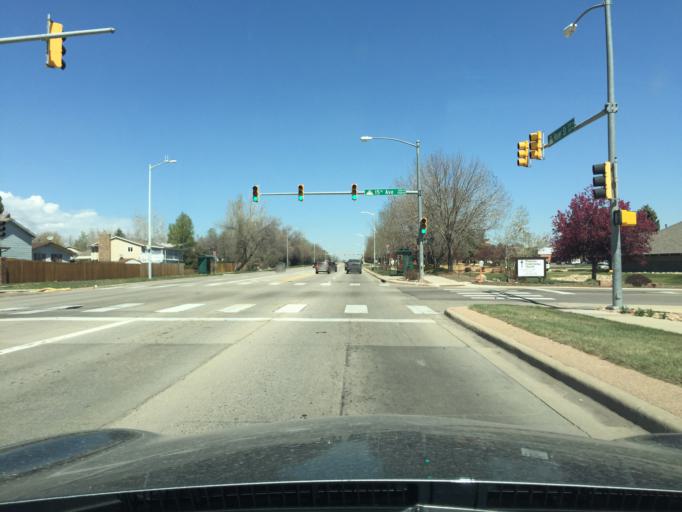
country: US
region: Colorado
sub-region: Boulder County
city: Longmont
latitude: 40.1847
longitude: -105.1308
